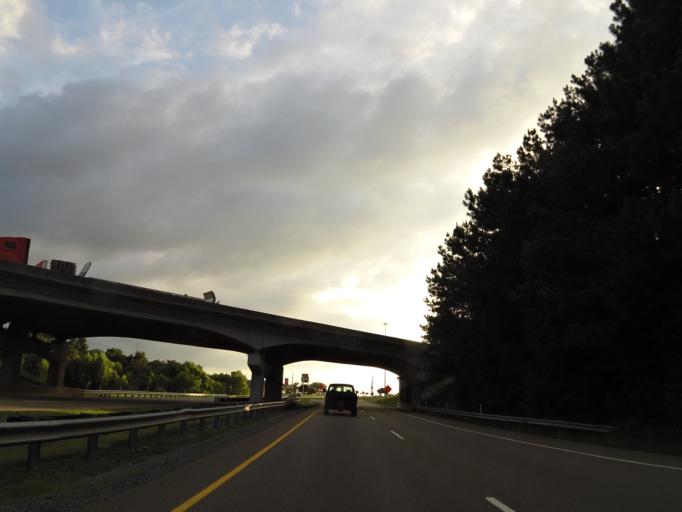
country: US
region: Tennessee
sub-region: Cocke County
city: Newport
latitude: 35.9700
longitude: -83.2573
